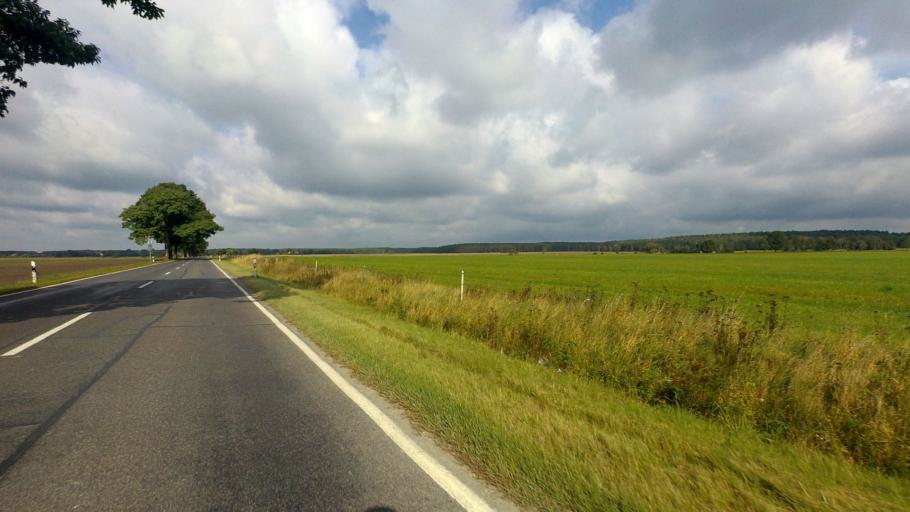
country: DE
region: Saxony
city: Wiednitz
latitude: 51.3935
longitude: 14.0163
